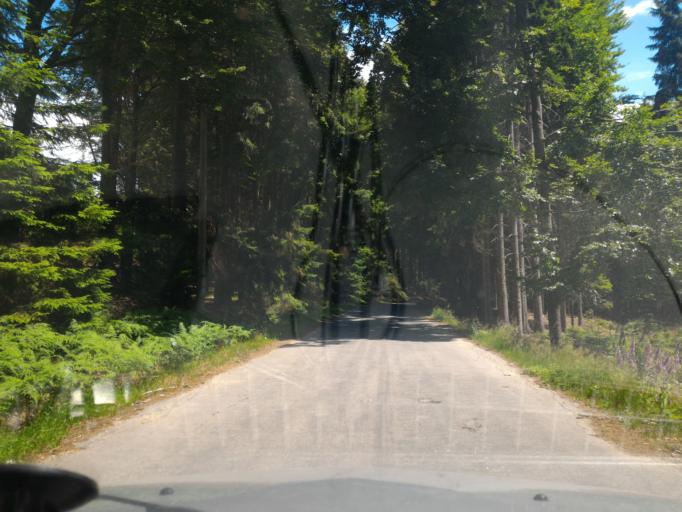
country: CZ
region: Vysocina
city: Batelov
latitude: 49.2313
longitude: 15.3785
